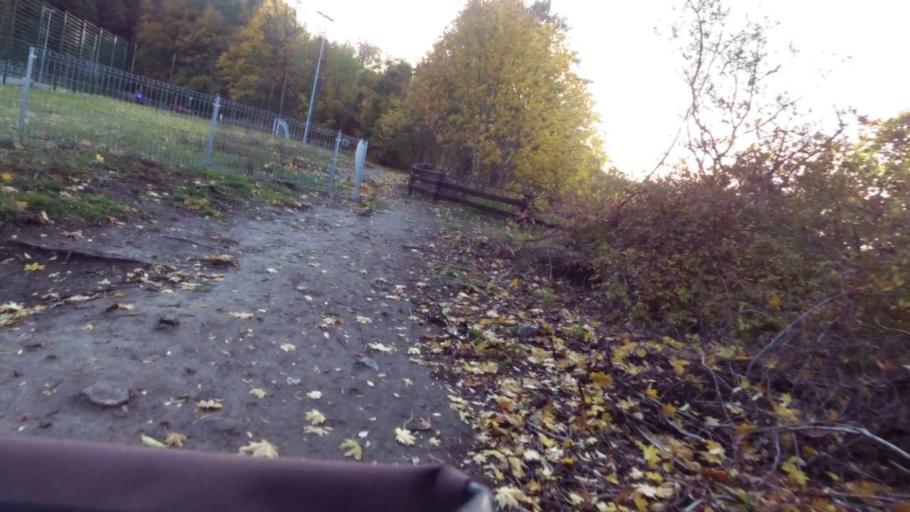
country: PL
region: West Pomeranian Voivodeship
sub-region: Powiat kamienski
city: Miedzyzdroje
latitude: 53.8777
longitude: 14.4424
